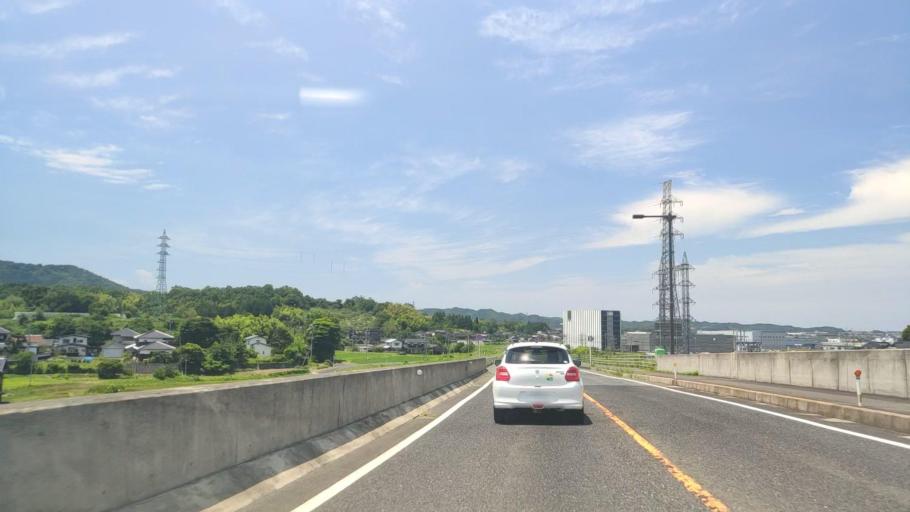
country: JP
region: Tottori
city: Tottori
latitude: 35.4492
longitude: 134.2528
